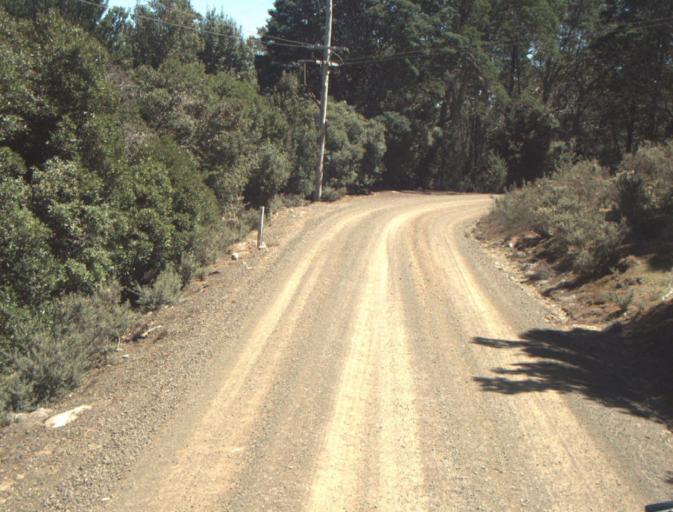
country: AU
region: Tasmania
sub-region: Dorset
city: Scottsdale
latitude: -41.3620
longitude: 147.4295
